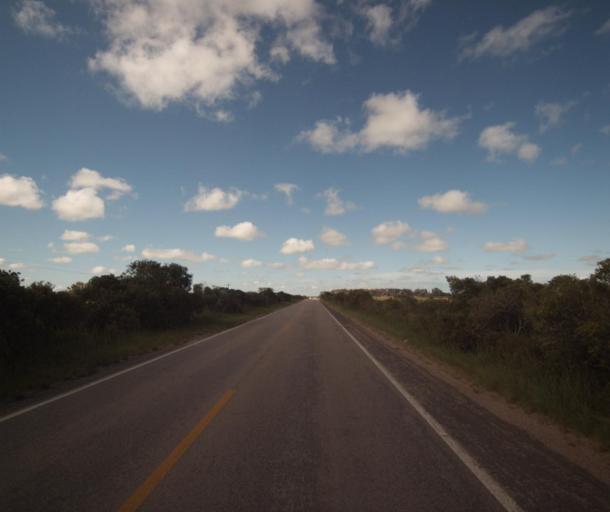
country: BR
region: Rio Grande do Sul
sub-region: Santa Vitoria Do Palmar
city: Santa Vitoria do Palmar
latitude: -33.4152
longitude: -53.2335
